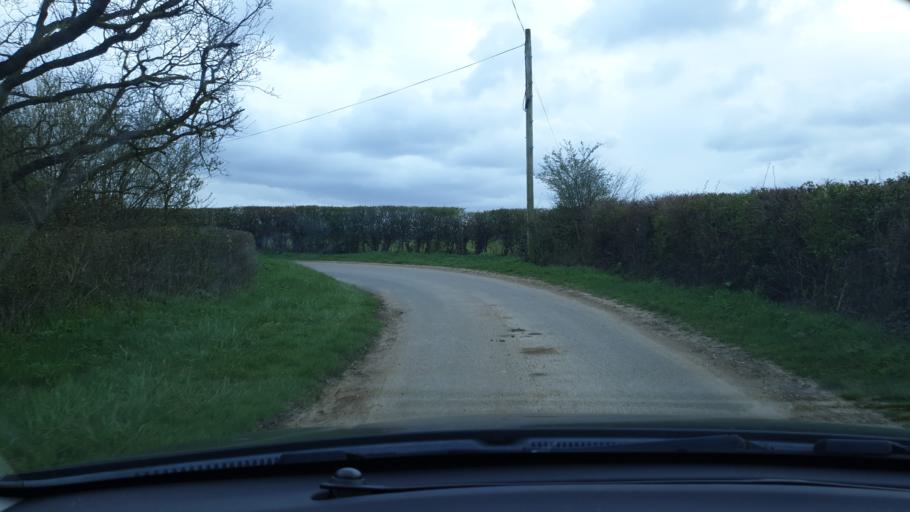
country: GB
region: England
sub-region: Essex
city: Mistley
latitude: 51.8965
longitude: 1.1323
